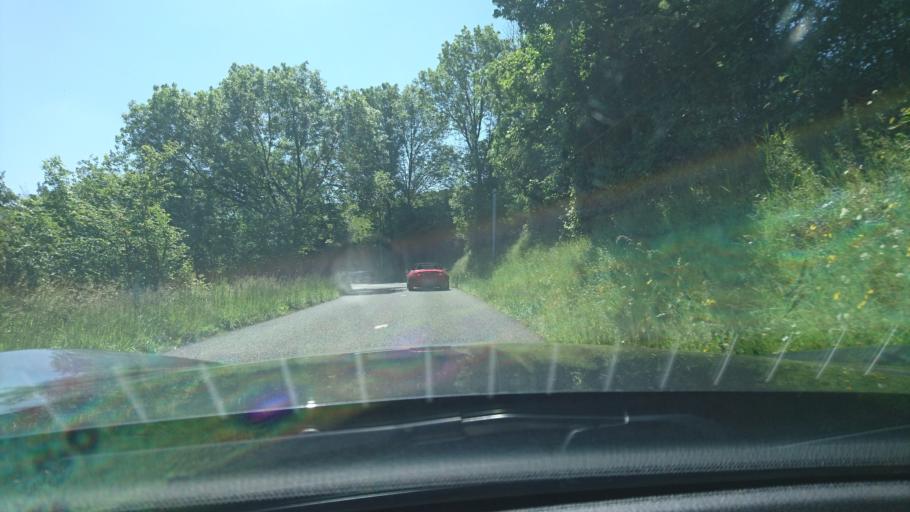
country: FR
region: Rhone-Alpes
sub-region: Departement de la Loire
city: Bussieres
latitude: 45.8772
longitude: 4.2840
